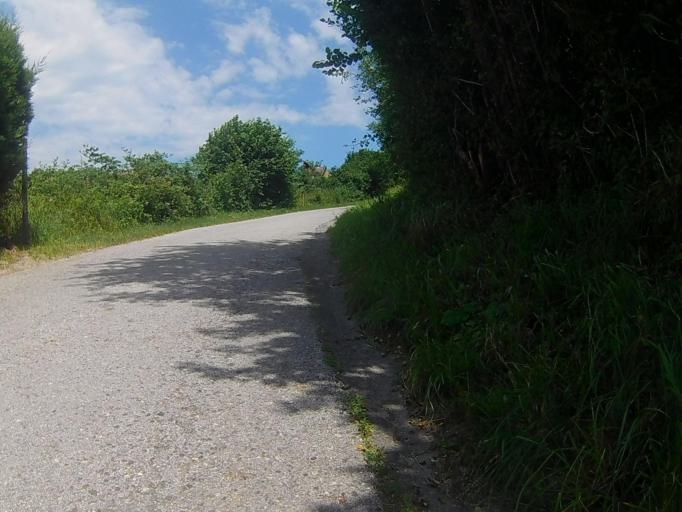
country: SI
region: Maribor
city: Kamnica
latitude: 46.5945
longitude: 15.6271
